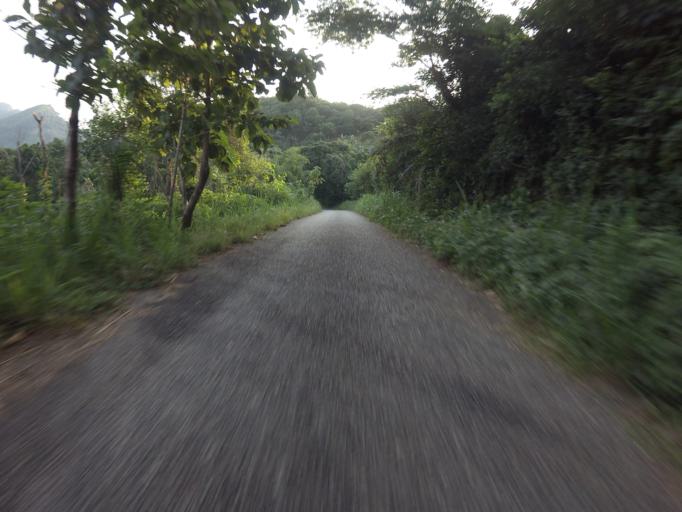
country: GH
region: Volta
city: Kpandu
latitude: 6.8855
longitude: 0.4448
